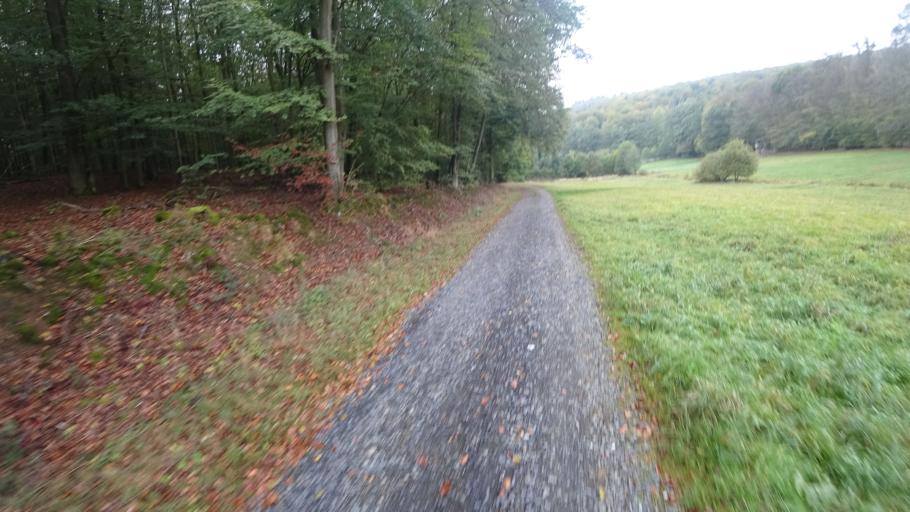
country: DE
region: Rheinland-Pfalz
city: Eppenrod
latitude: 50.4117
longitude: 7.9278
